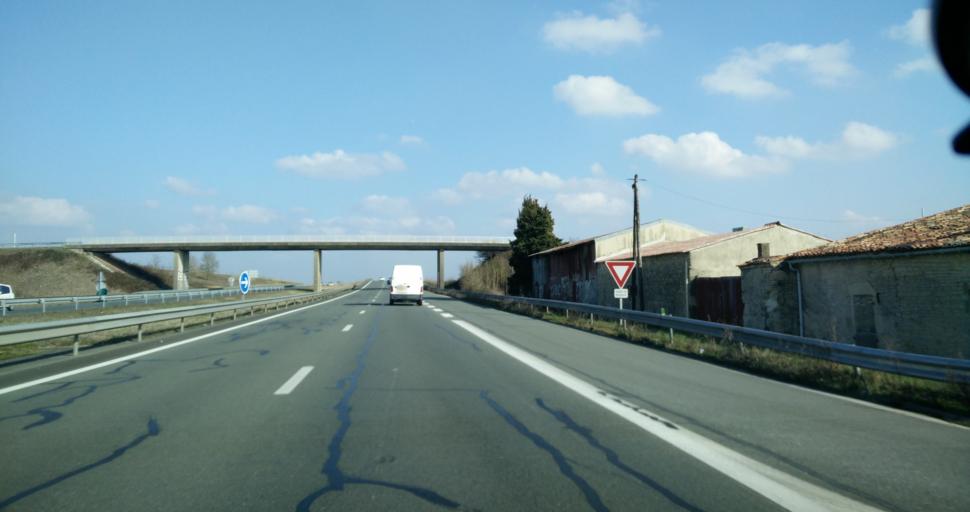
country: FR
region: Poitou-Charentes
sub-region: Departement de la Charente-Maritime
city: Verines
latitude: 46.2138
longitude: -0.9908
